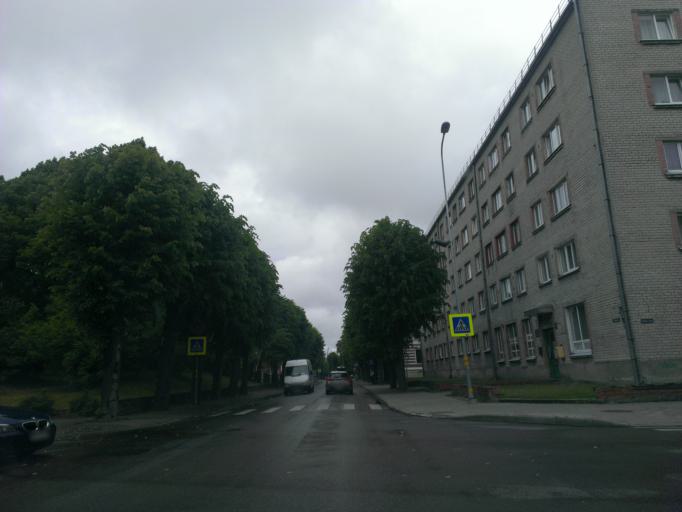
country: LV
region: Liepaja
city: Liepaja
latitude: 56.5084
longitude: 20.9999
